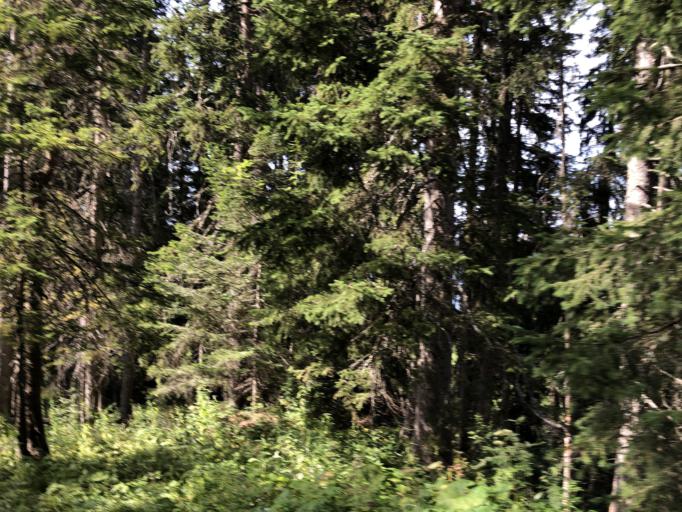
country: FR
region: Rhone-Alpes
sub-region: Departement de la Haute-Savoie
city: Combloux
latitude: 45.8707
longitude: 6.6614
